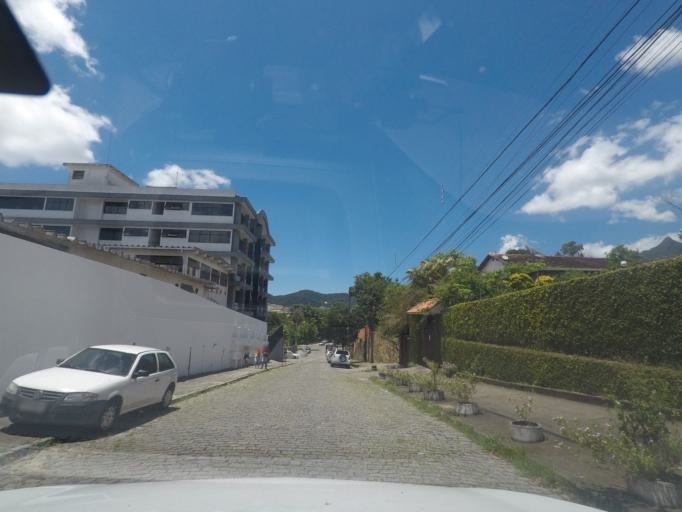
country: BR
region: Rio de Janeiro
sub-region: Teresopolis
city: Teresopolis
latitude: -22.4339
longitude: -42.9798
